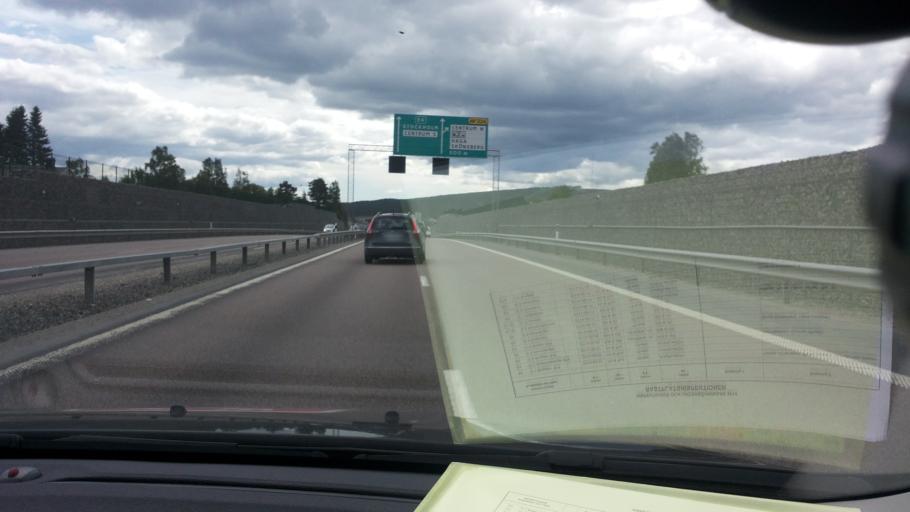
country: SE
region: Vaesternorrland
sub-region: Sundsvalls Kommun
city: Sundsvall
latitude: 62.4050
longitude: 17.3369
